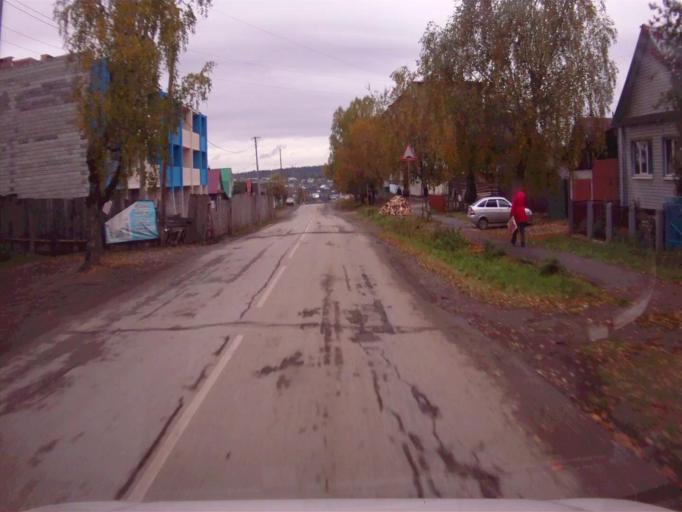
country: RU
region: Chelyabinsk
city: Nyazepetrovsk
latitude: 56.0558
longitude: 59.6057
